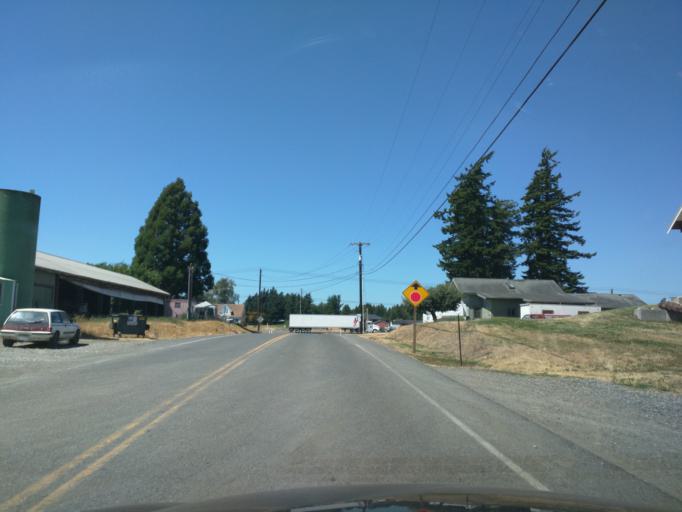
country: US
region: Washington
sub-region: Whatcom County
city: Lynden
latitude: 48.8843
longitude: -122.4836
